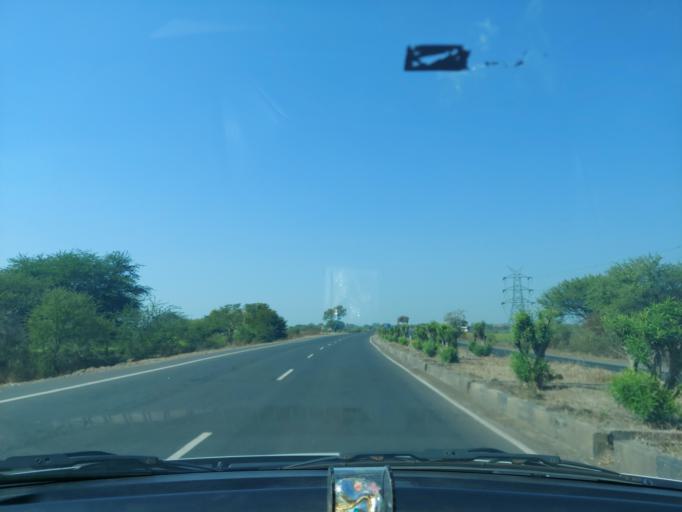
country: IN
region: Madhya Pradesh
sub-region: Indore
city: Manpur
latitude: 22.5041
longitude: 75.5523
